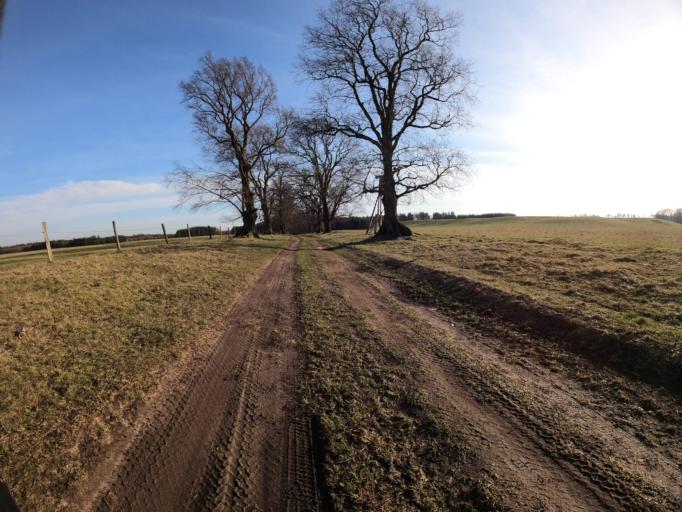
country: PL
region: West Pomeranian Voivodeship
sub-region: Powiat koszalinski
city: Polanow
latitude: 54.1956
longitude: 16.6594
